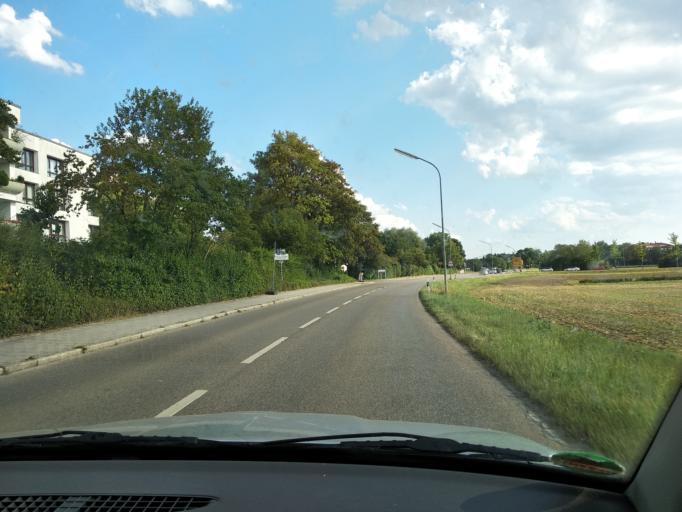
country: DE
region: Bavaria
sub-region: Upper Bavaria
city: Taufkirchen
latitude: 48.0553
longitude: 11.6190
